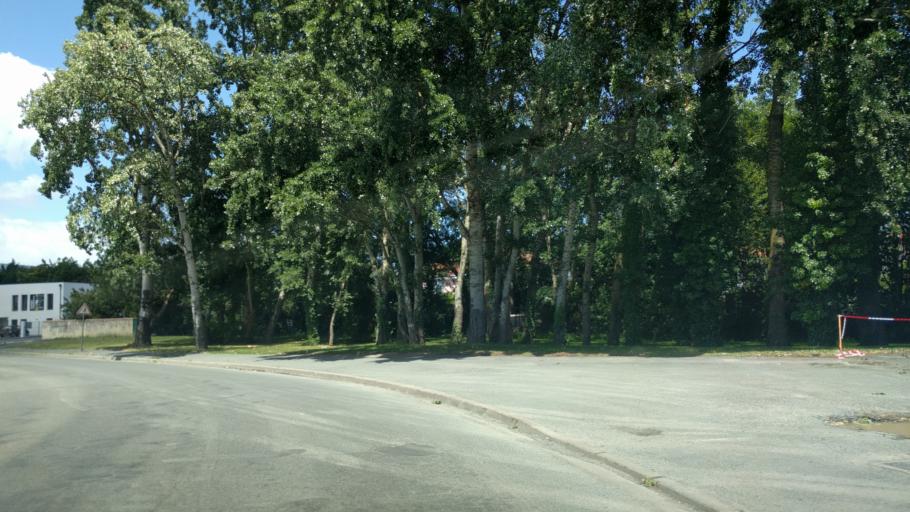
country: FR
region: Poitou-Charentes
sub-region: Departement de la Charente-Maritime
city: Puilboreau
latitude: 46.1634
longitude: -1.1245
